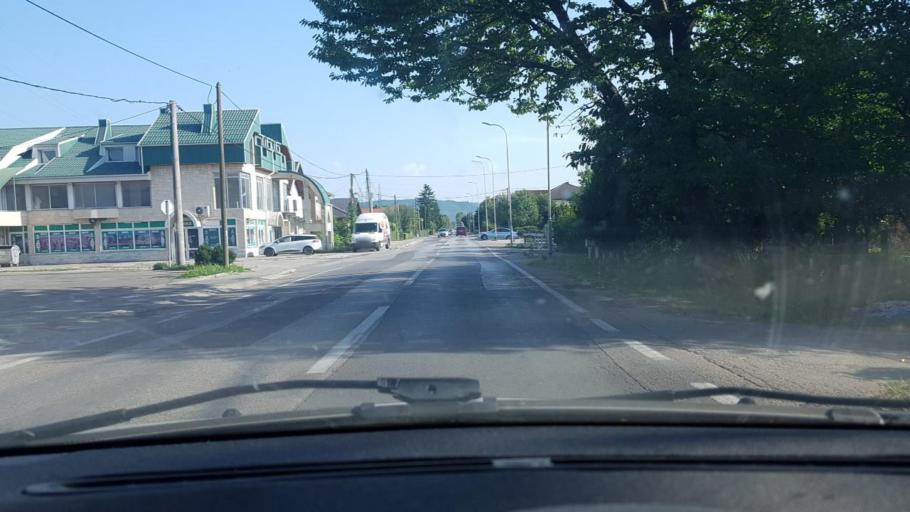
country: BA
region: Federation of Bosnia and Herzegovina
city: Bihac
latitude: 44.8261
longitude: 15.8817
